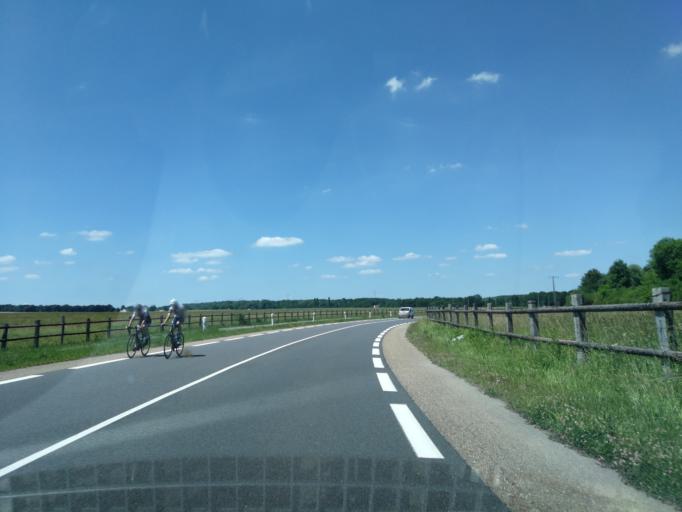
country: FR
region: Ile-de-France
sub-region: Departement de l'Essonne
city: Briis-sous-Forges
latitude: 48.6175
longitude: 2.1183
